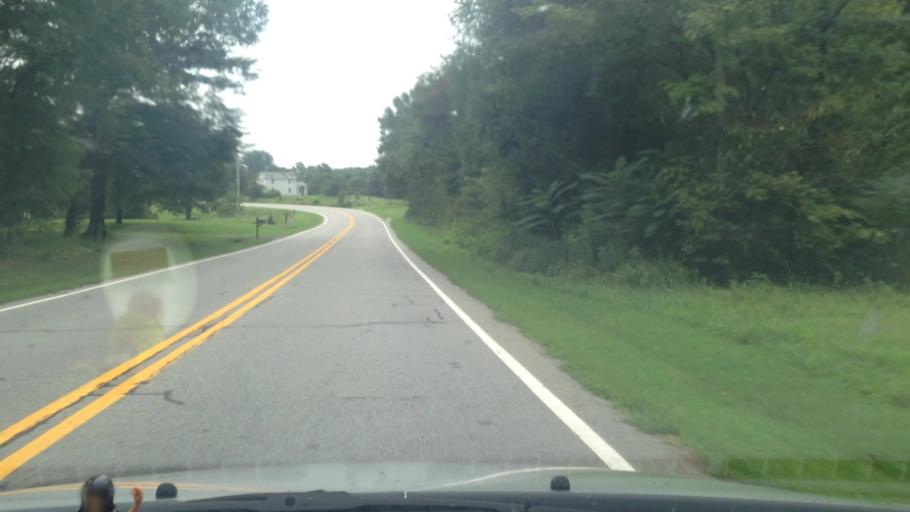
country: US
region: North Carolina
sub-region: Stokes County
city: Danbury
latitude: 36.4236
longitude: -80.1099
